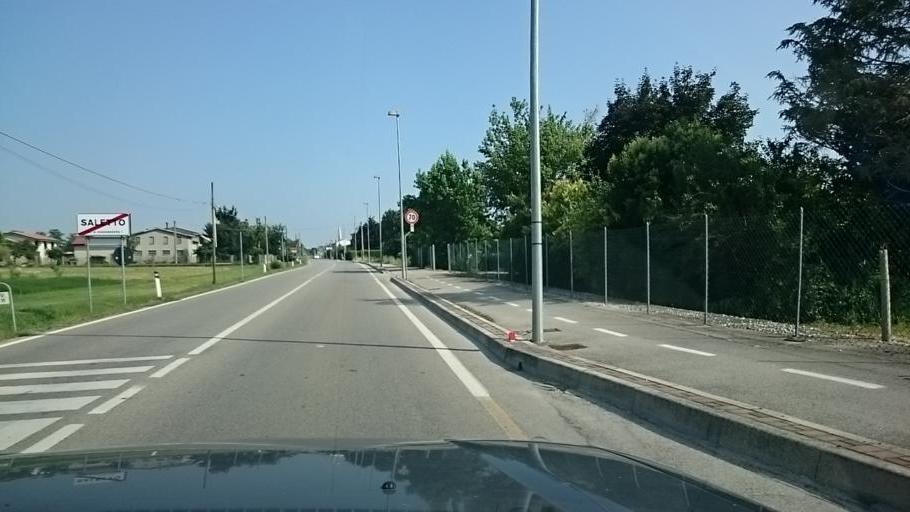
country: IT
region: Veneto
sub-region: Provincia di Padova
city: Saletto
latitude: 45.4679
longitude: 11.8660
